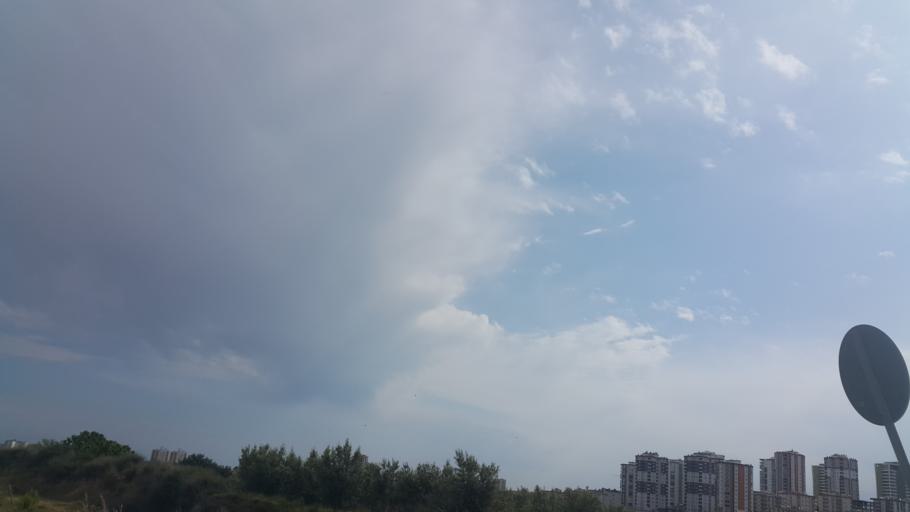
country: TR
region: Mersin
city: Tarsus
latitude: 36.9462
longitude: 34.8589
